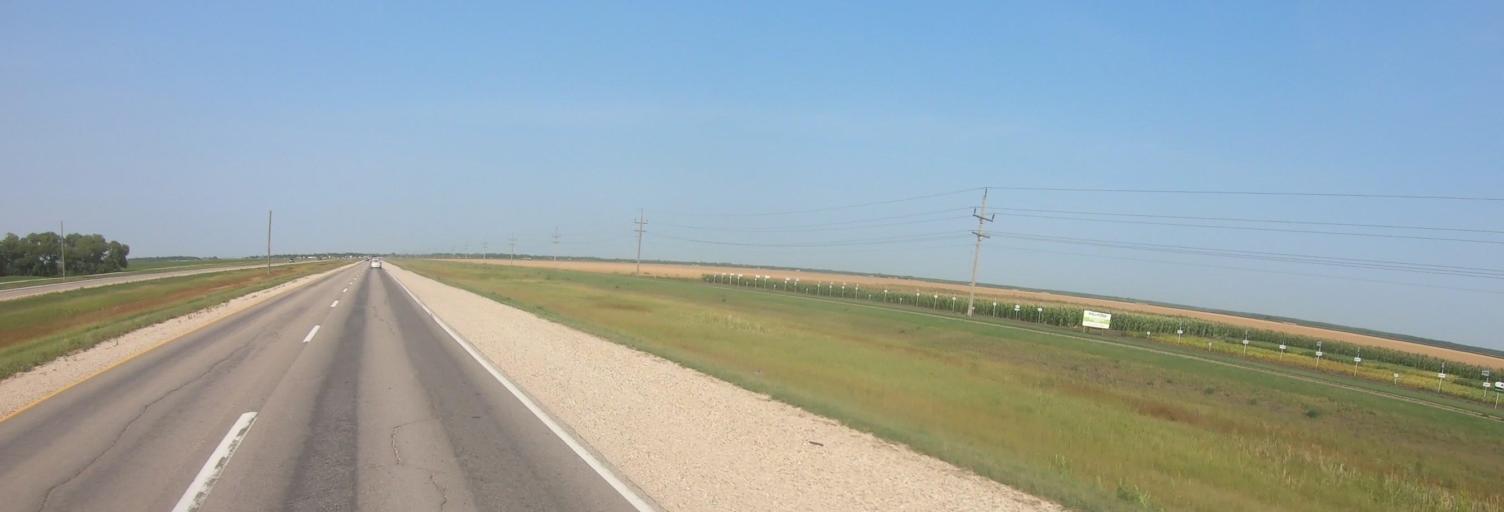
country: CA
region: Manitoba
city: Steinbach
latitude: 49.6441
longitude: -96.6824
